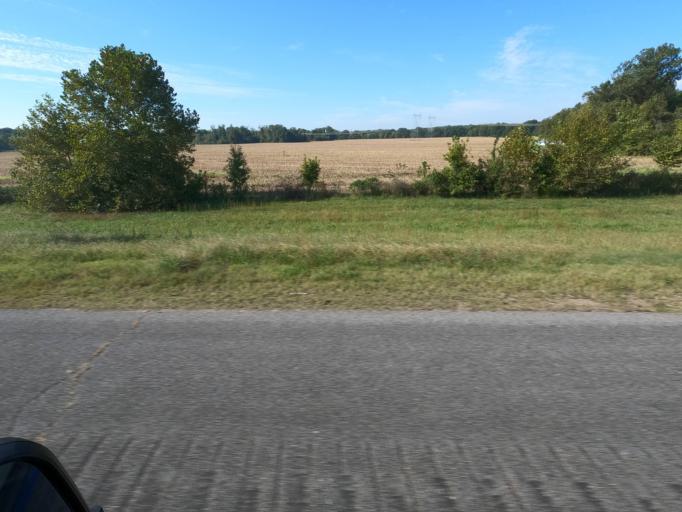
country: US
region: Tennessee
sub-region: Shelby County
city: Arlington
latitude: 35.3006
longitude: -89.6956
